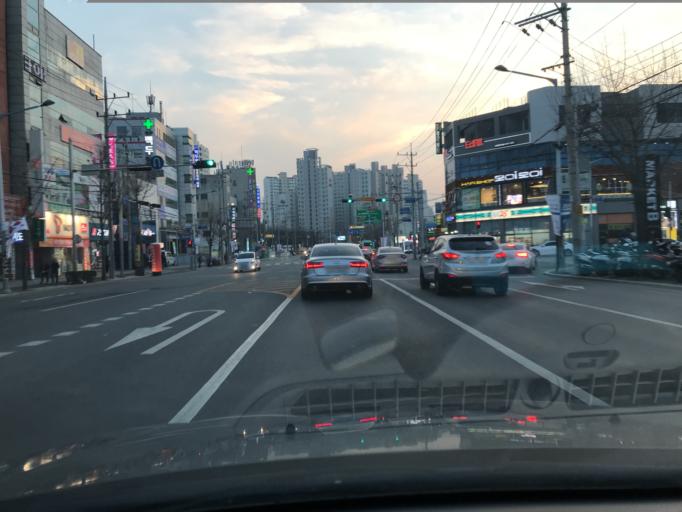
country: KR
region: Daegu
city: Hwawon
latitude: 35.8123
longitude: 128.5181
